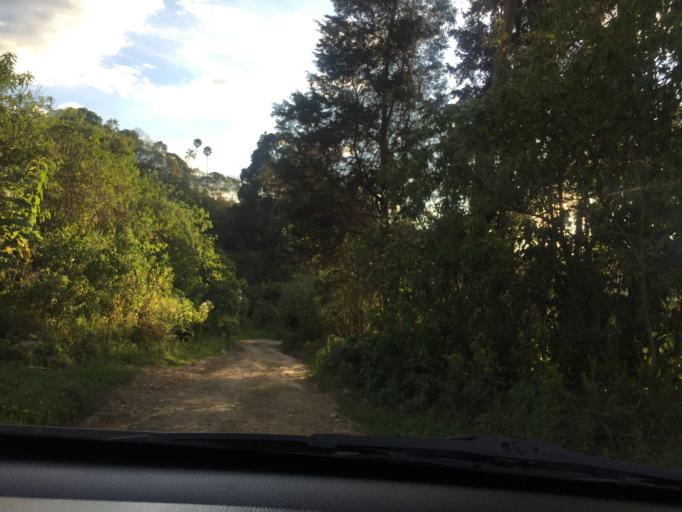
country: CO
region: Cundinamarca
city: Zipacon
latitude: 4.7191
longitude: -74.3914
